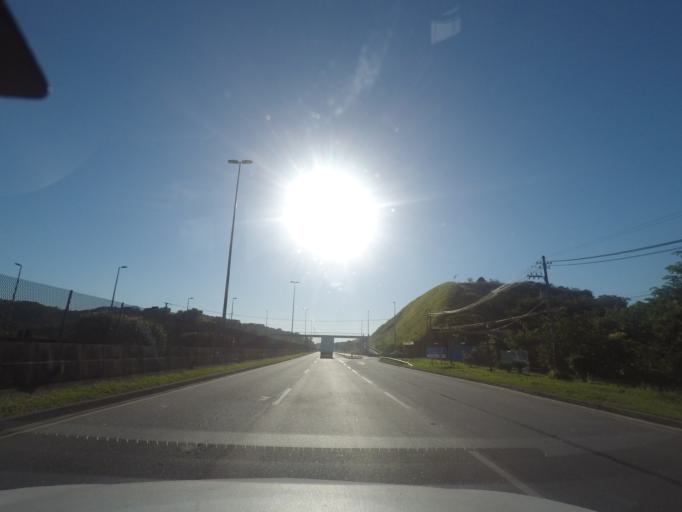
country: BR
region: Rio de Janeiro
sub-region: Petropolis
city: Petropolis
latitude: -22.6512
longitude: -43.1669
